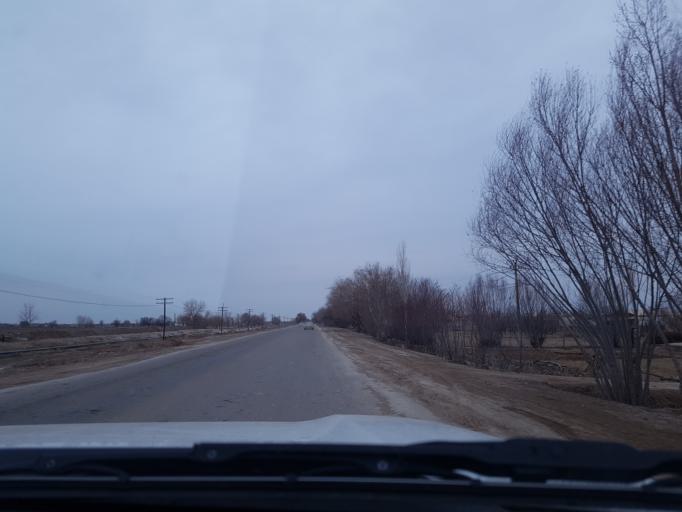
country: TM
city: Akdepe
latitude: 41.9815
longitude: 59.4681
